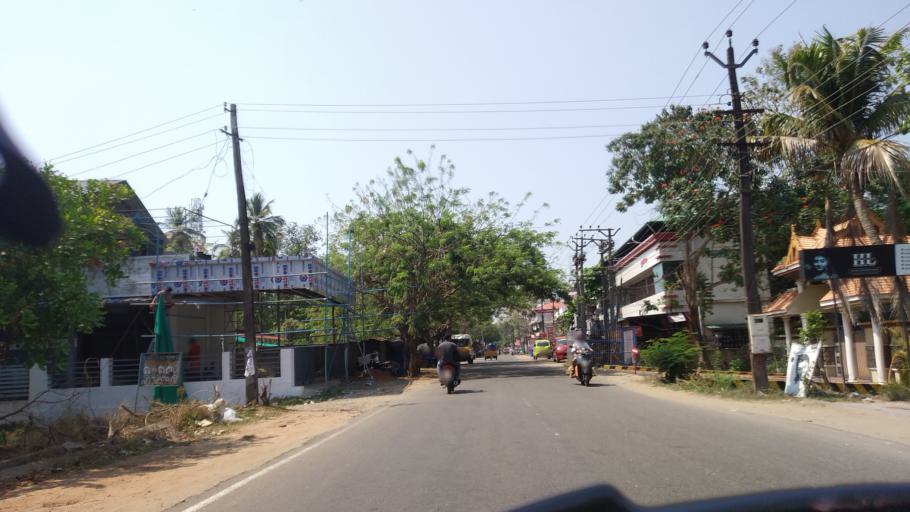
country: IN
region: Kerala
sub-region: Thrissur District
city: Kodungallur
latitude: 10.2094
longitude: 76.1633
